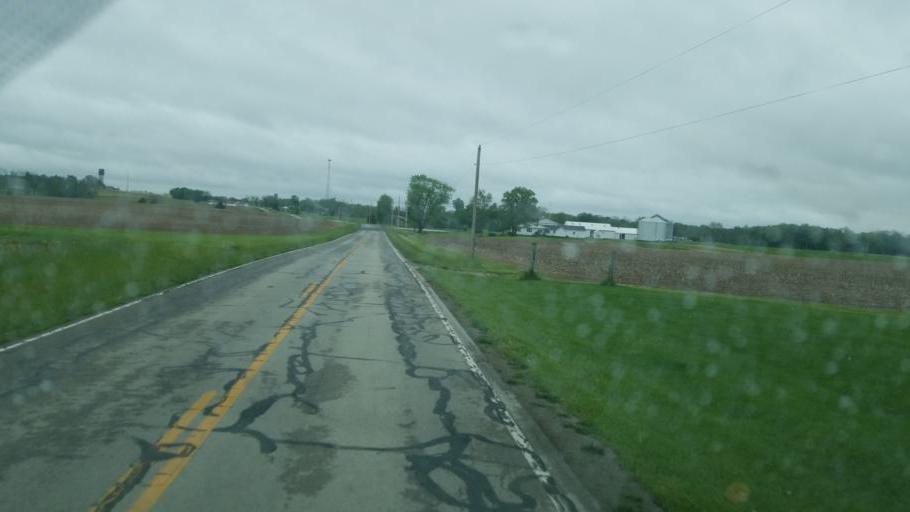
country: US
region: Ohio
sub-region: Highland County
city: Leesburg
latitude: 39.3236
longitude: -83.5573
